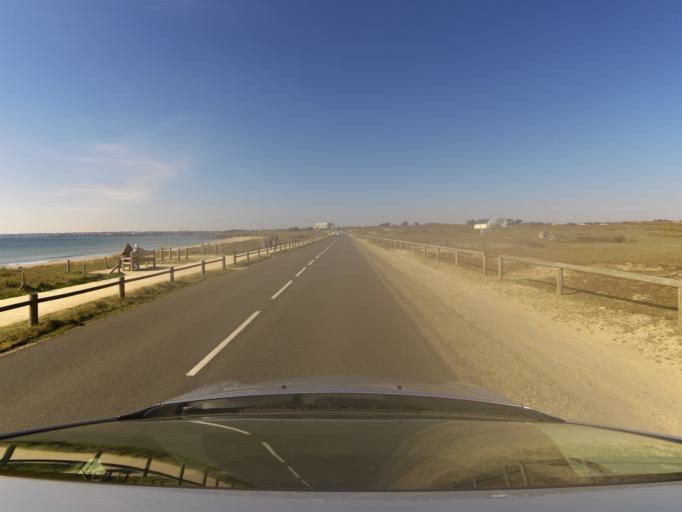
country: FR
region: Brittany
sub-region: Departement du Morbihan
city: Guidel-Plage
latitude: 47.7436
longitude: -3.5037
